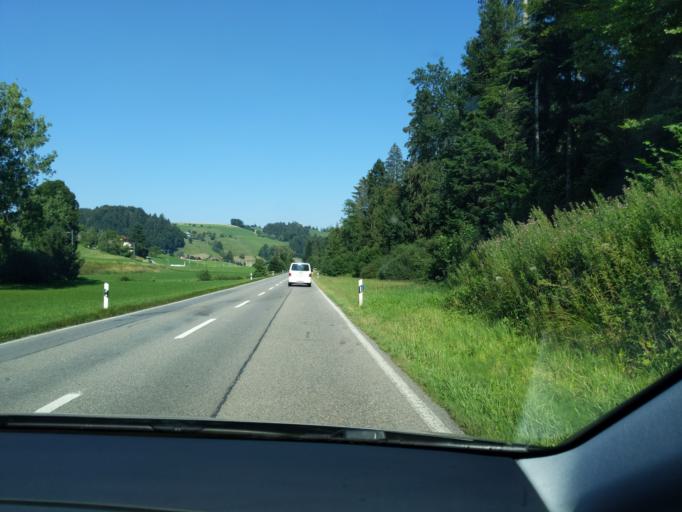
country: CH
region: Bern
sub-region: Oberaargau
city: Huttwil
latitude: 47.1242
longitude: 7.8742
